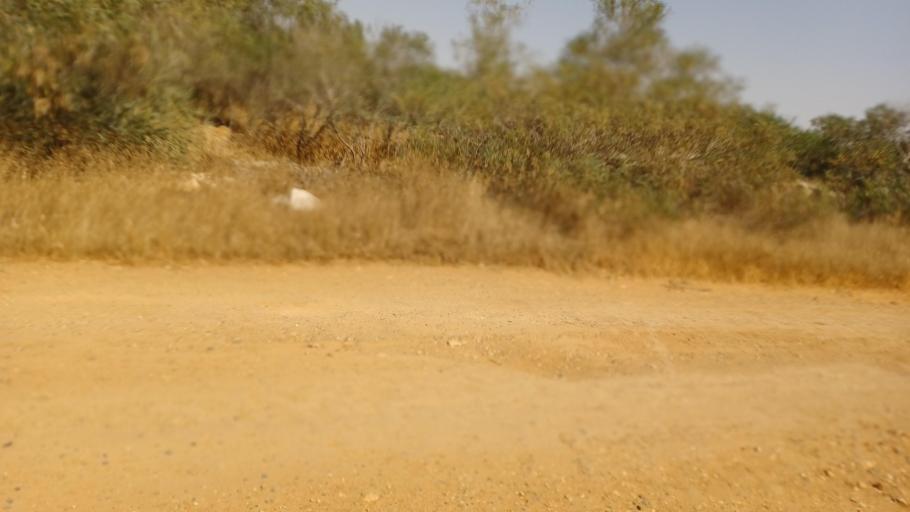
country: CY
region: Ammochostos
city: Liopetri
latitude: 34.9795
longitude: 33.8763
